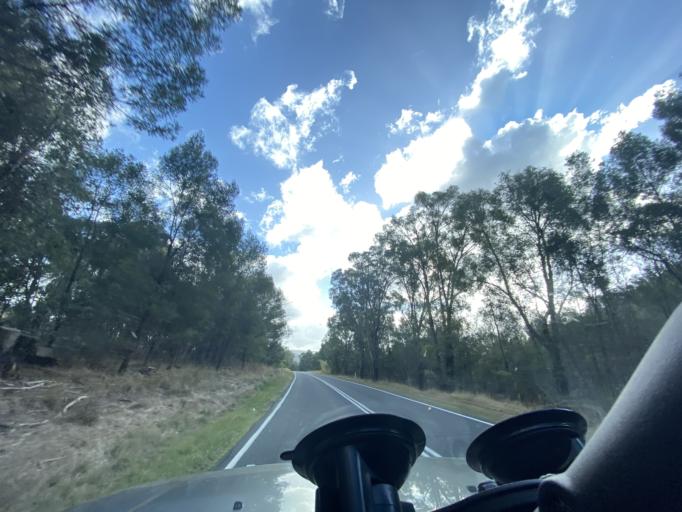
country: AU
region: Victoria
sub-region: Murrindindi
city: Kinglake West
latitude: -37.3223
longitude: 145.3127
